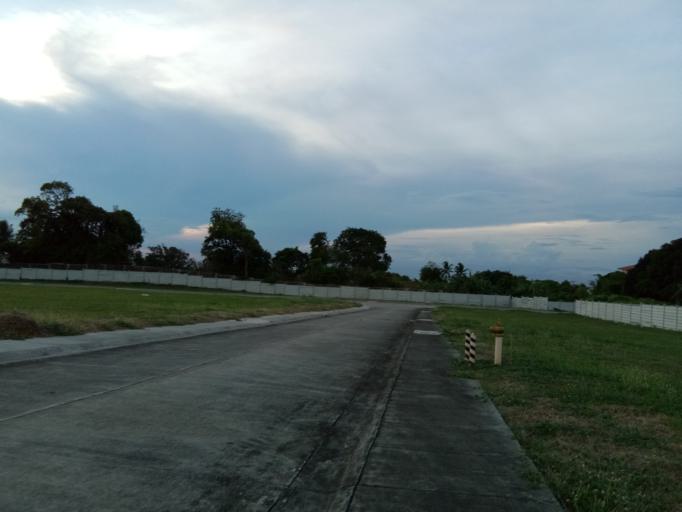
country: PH
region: Calabarzon
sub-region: Province of Cavite
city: Biga
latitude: 14.2758
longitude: 120.9663
